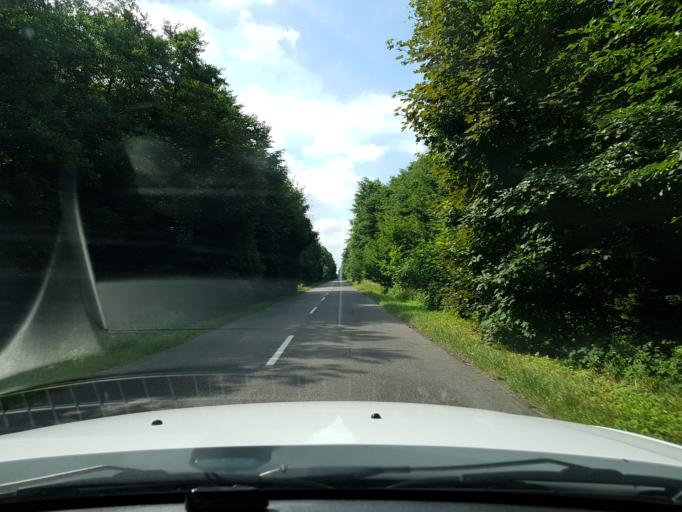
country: PL
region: West Pomeranian Voivodeship
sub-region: Powiat gryfinski
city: Banie
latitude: 53.0138
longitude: 14.7215
